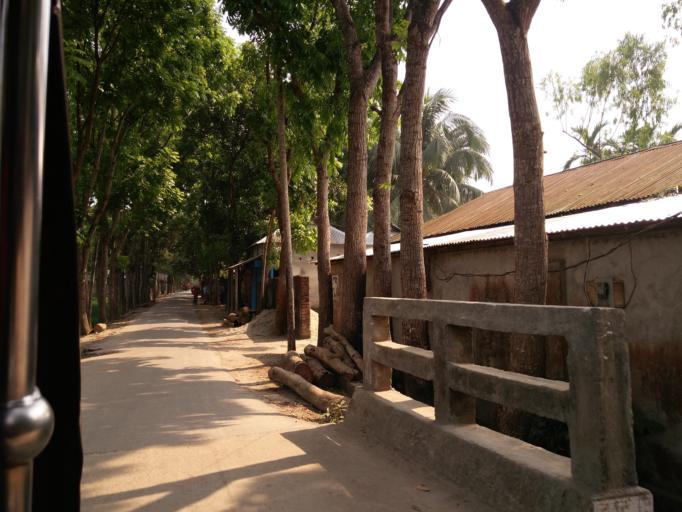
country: BD
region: Dhaka
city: Muktagacha
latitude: 24.9133
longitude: 90.2160
